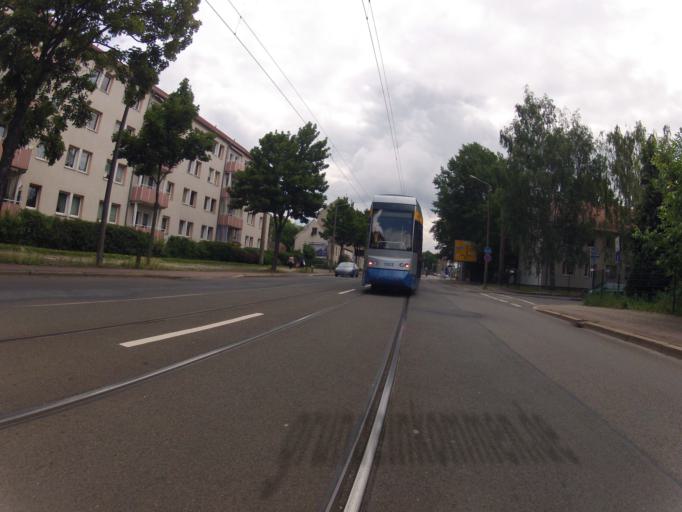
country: DE
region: Saxony
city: Taucha
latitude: 51.3462
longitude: 12.4427
